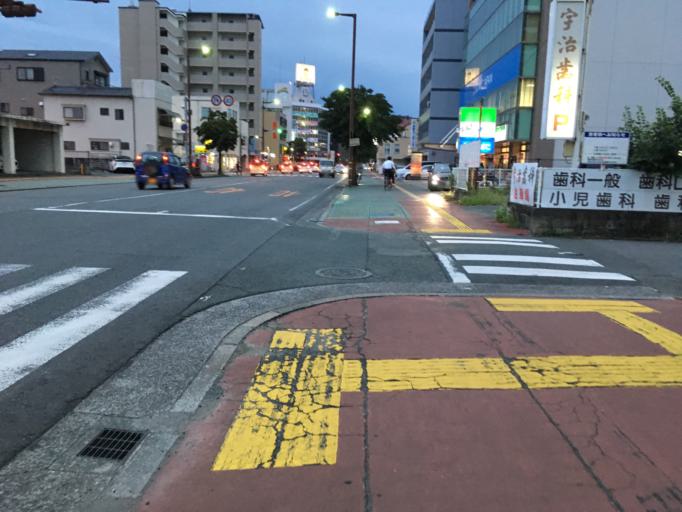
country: JP
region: Kumamoto
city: Kumamoto
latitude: 32.7962
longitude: 130.7266
